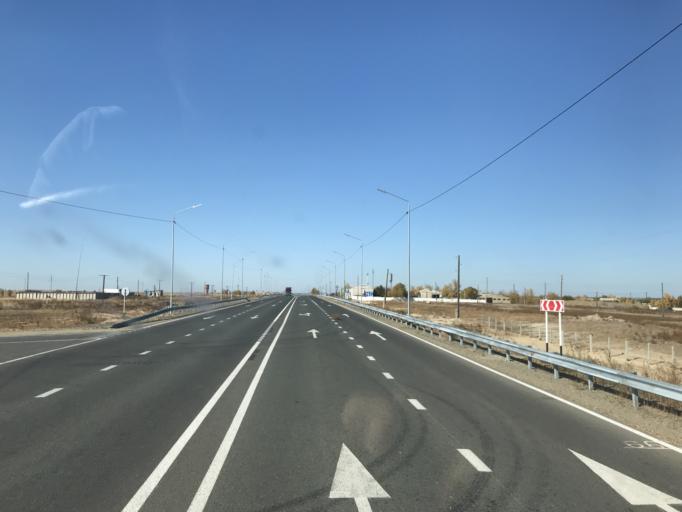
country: RU
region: Altai Krai
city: Malinovoye Ozero
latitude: 50.8747
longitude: 79.4828
